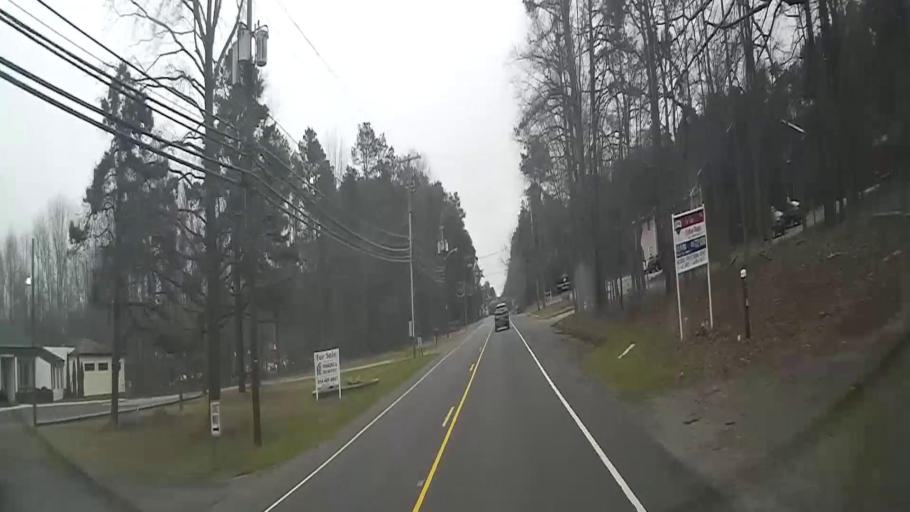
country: US
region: New Jersey
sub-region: Burlington County
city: Medford Lakes
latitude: 39.8727
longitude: -74.8488
